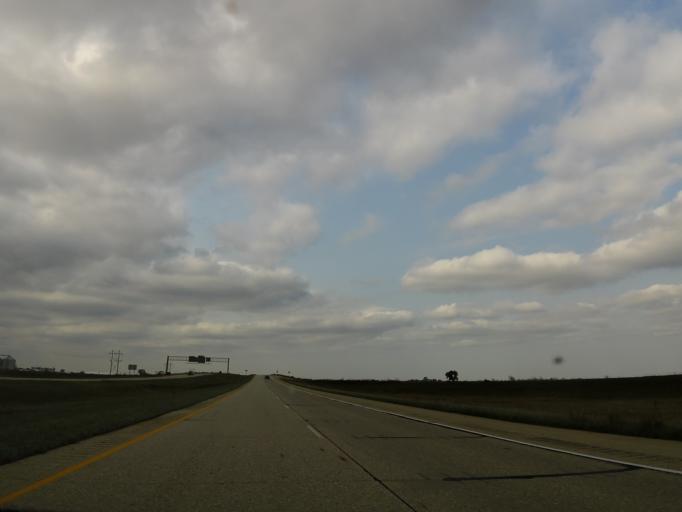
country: US
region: North Dakota
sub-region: Richland County
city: Wahpeton
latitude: 46.2634
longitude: -96.8338
